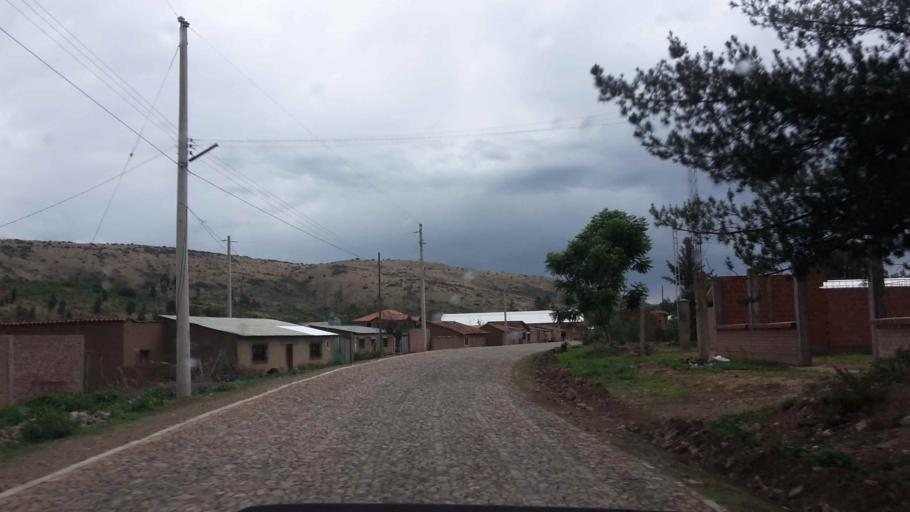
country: BO
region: Cochabamba
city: Cochabamba
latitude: -17.5497
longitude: -66.1755
